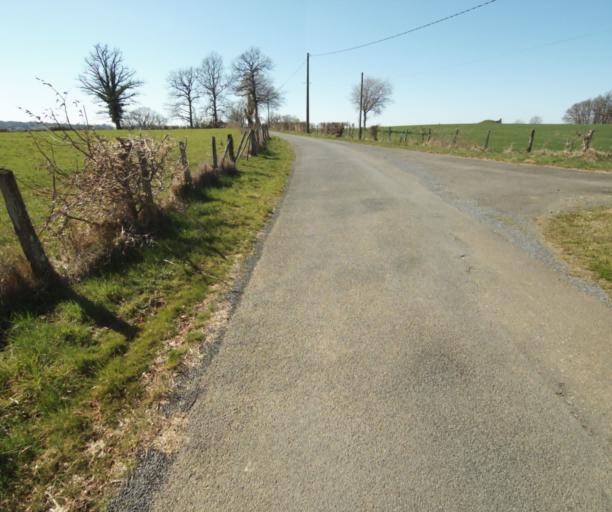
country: FR
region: Limousin
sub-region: Departement de la Correze
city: Uzerche
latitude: 45.4148
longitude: 1.6255
